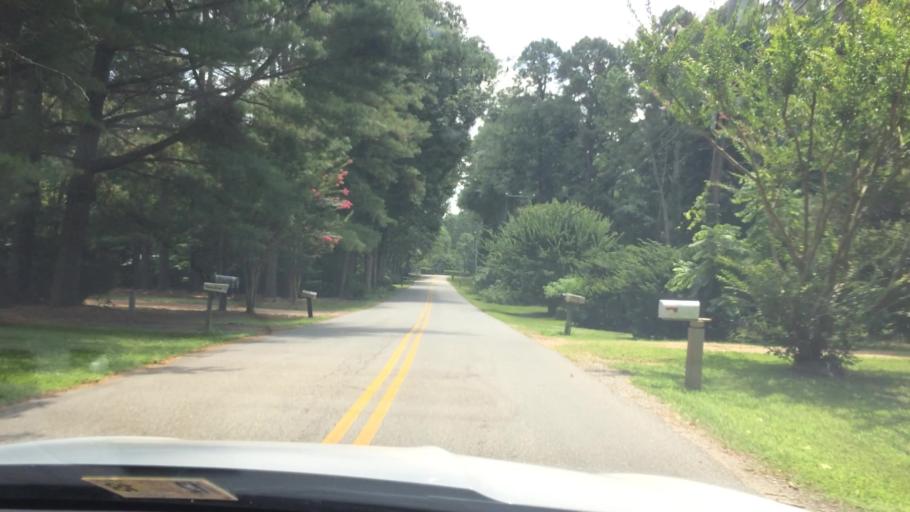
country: US
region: Virginia
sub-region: York County
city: Yorktown
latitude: 37.2061
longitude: -76.4831
